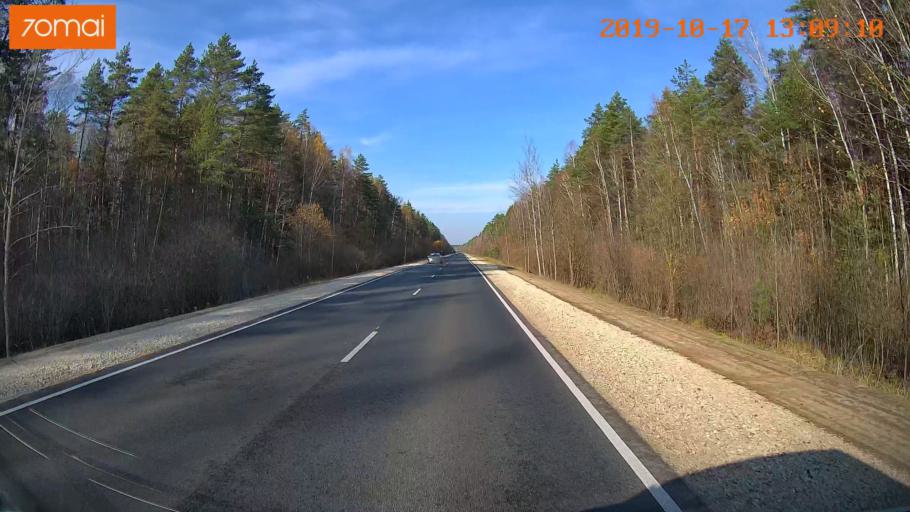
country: RU
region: Rjazan
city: Syntul
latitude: 54.9998
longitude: 41.2647
